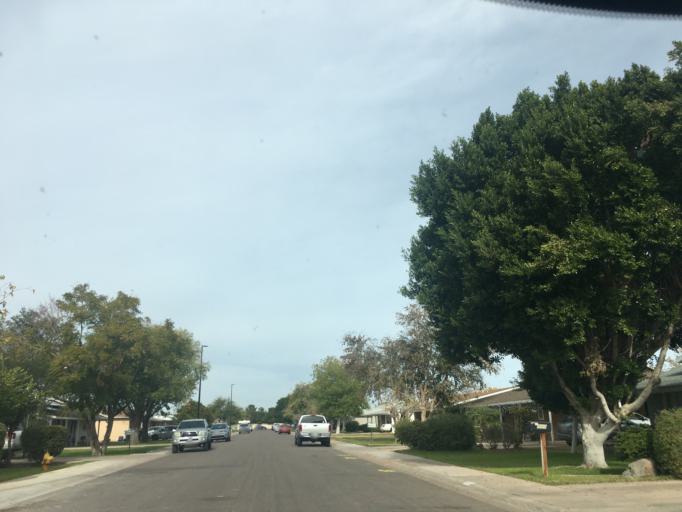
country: US
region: Arizona
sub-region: Maricopa County
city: Gilbert
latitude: 33.3479
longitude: -111.7953
